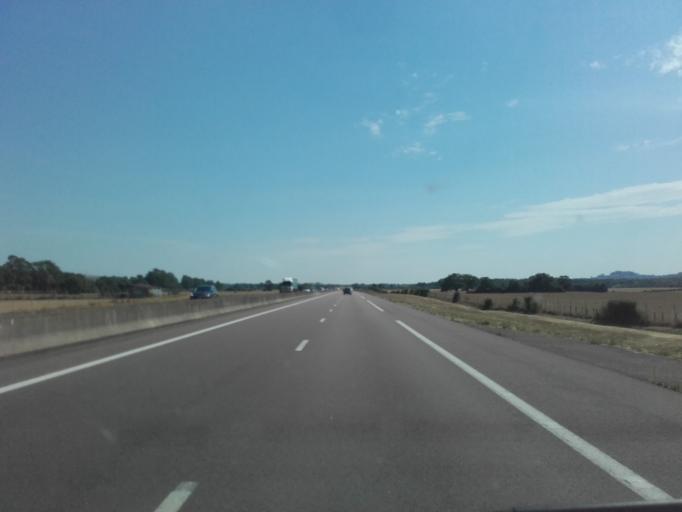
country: FR
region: Bourgogne
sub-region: Departement de la Cote-d'Or
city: Pouilly-en-Auxois
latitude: 47.2876
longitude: 4.5075
